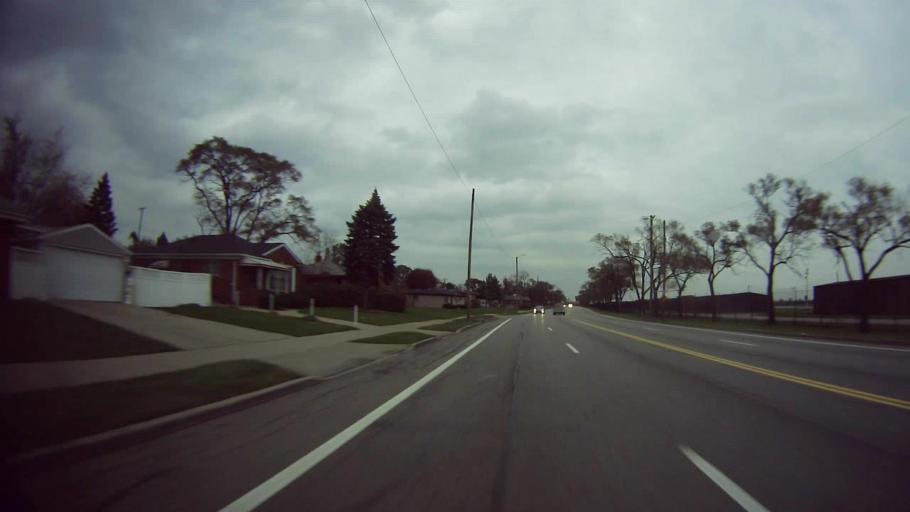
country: US
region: Michigan
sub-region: Wayne County
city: Hamtramck
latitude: 42.4177
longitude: -83.0117
